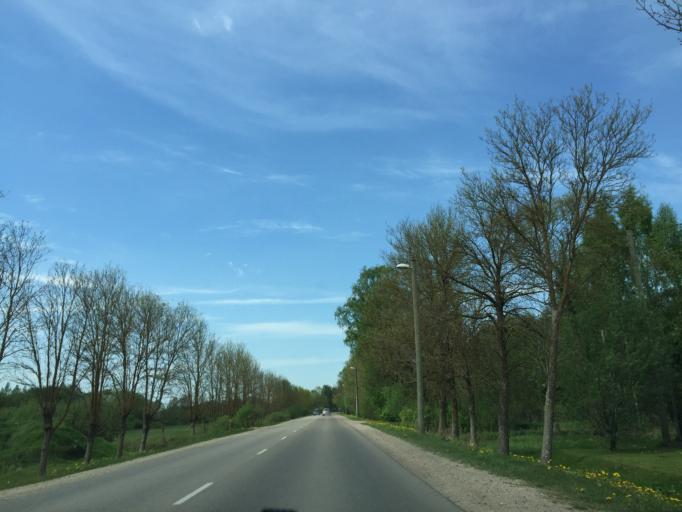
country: LV
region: Jelgava
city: Jelgava
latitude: 56.6756
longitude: 23.7259
